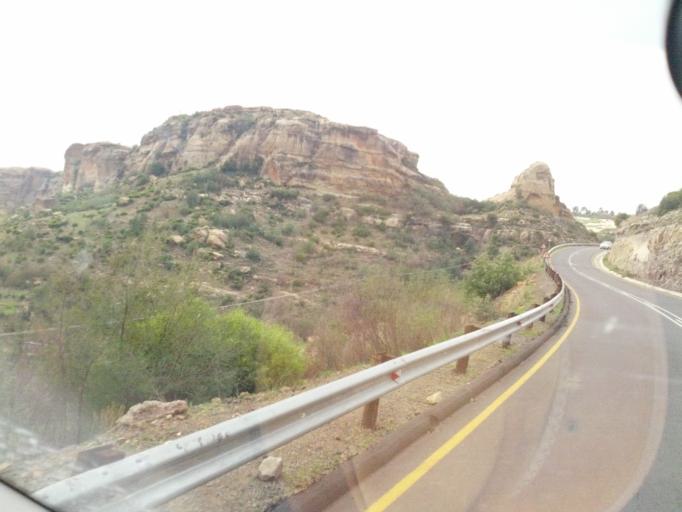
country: LS
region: Maseru
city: Nako
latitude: -29.4795
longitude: 27.7396
